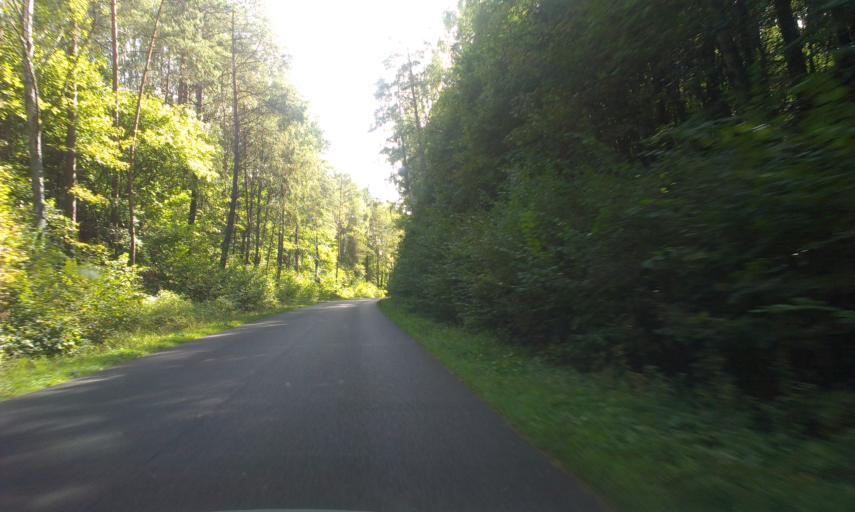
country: PL
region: Greater Poland Voivodeship
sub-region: Powiat zlotowski
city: Zlotow
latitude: 53.4889
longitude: 16.9895
